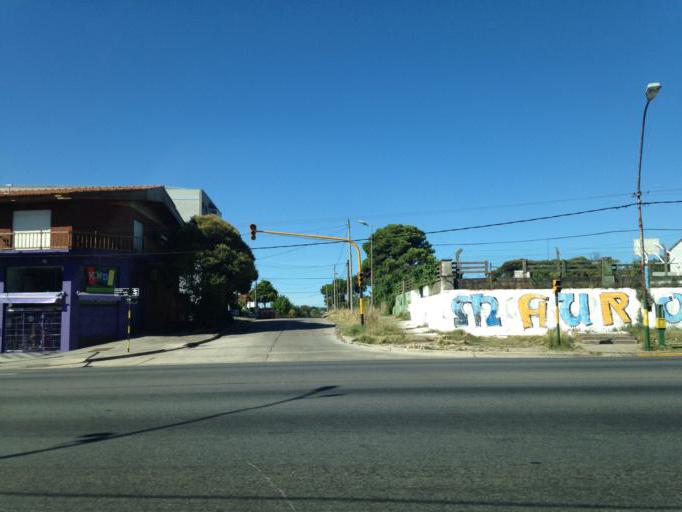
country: AR
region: Buenos Aires
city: Mar del Plata
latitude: -38.0350
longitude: -57.5503
